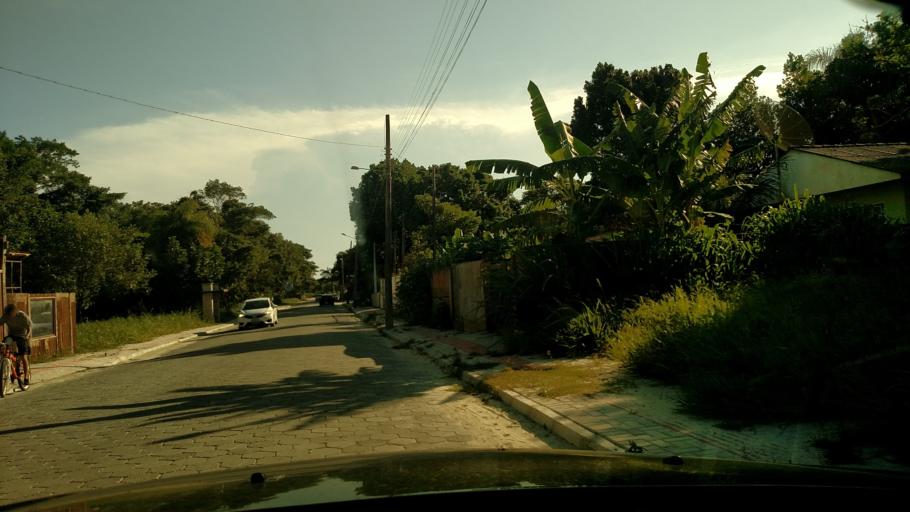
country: BR
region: Santa Catarina
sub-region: Porto Belo
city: Porto Belo
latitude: -27.1807
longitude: -48.5090
